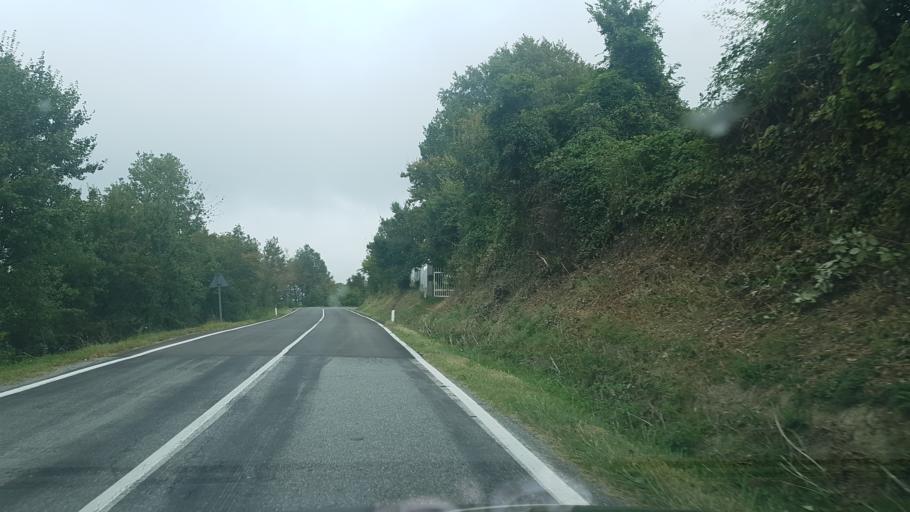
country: IT
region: Piedmont
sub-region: Provincia di Cuneo
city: Paroldo
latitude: 44.4195
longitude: 8.0924
